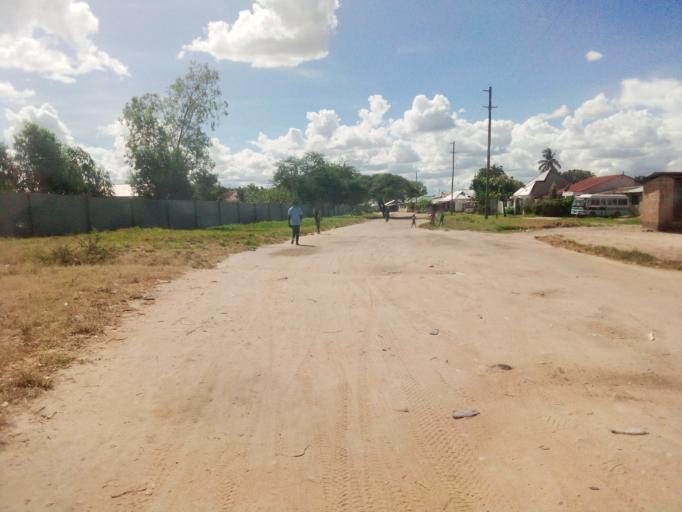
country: TZ
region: Dodoma
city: Dodoma
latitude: -6.1783
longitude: 35.7559
